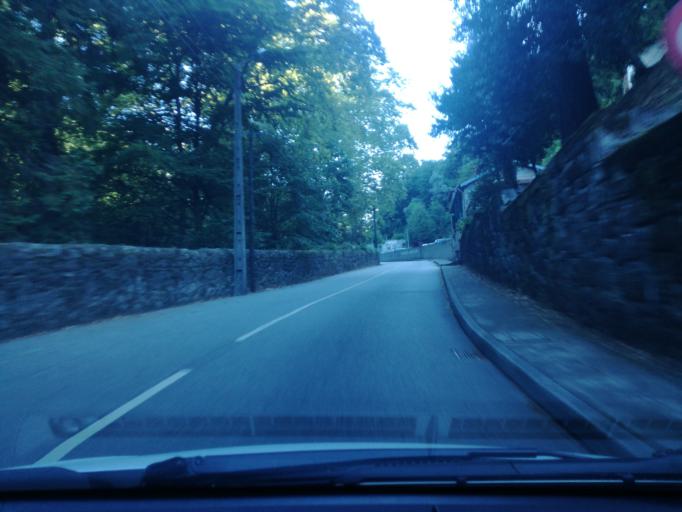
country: PT
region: Braga
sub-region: Vieira do Minho
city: Real
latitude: 41.7307
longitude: -8.1617
